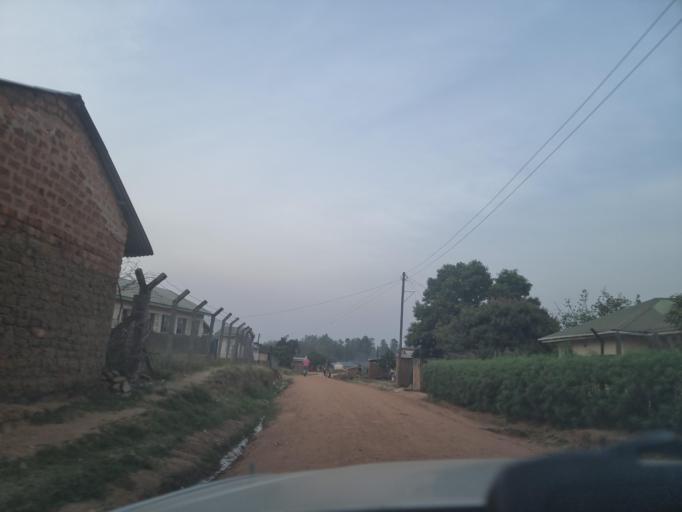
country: UG
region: Northern Region
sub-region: Arua District
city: Arua
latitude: 3.0332
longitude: 30.9110
